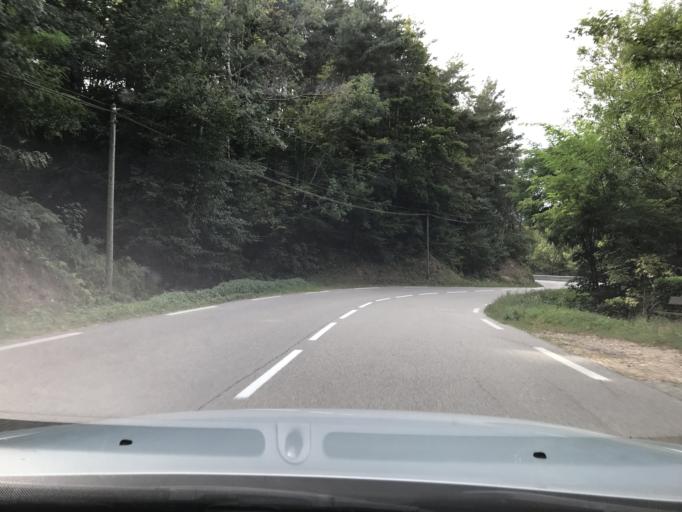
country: FR
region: Rhone-Alpes
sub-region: Departement de l'Ardeche
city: Lamastre
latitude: 44.9834
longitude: 4.5975
